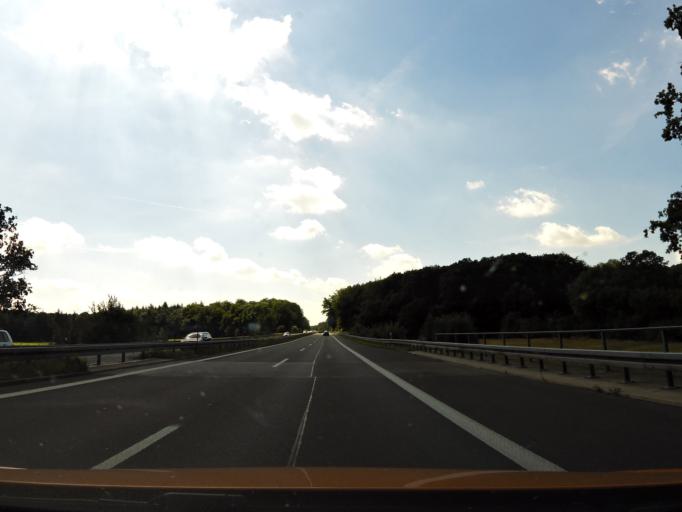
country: DE
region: Brandenburg
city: Gramzow
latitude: 53.1954
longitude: 13.9402
